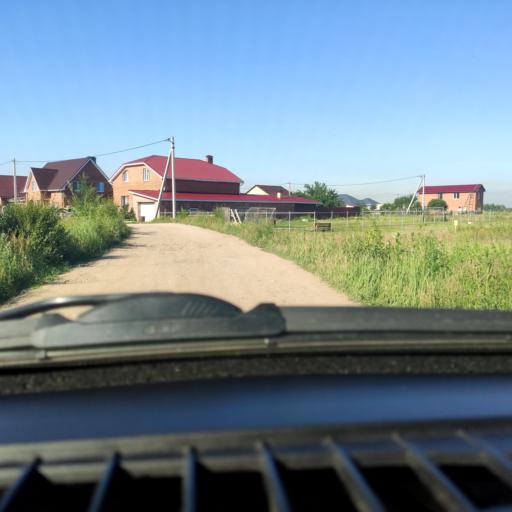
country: RU
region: Samara
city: Tol'yatti
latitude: 53.5607
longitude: 49.3785
